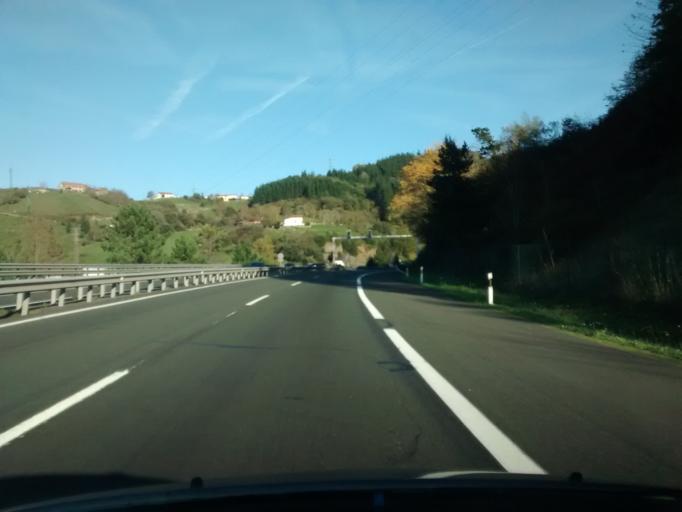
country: ES
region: Basque Country
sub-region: Bizkaia
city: Zaldibar
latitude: 43.1711
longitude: -2.5388
